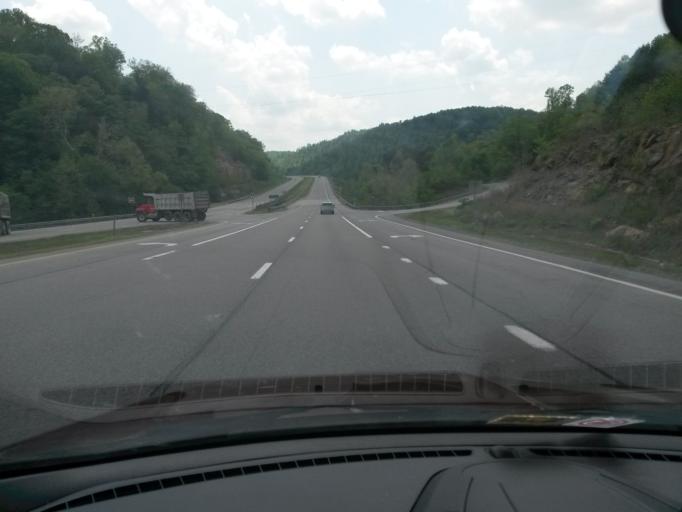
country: US
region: West Virginia
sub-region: Braxton County
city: Sutton
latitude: 38.5784
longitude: -80.7377
